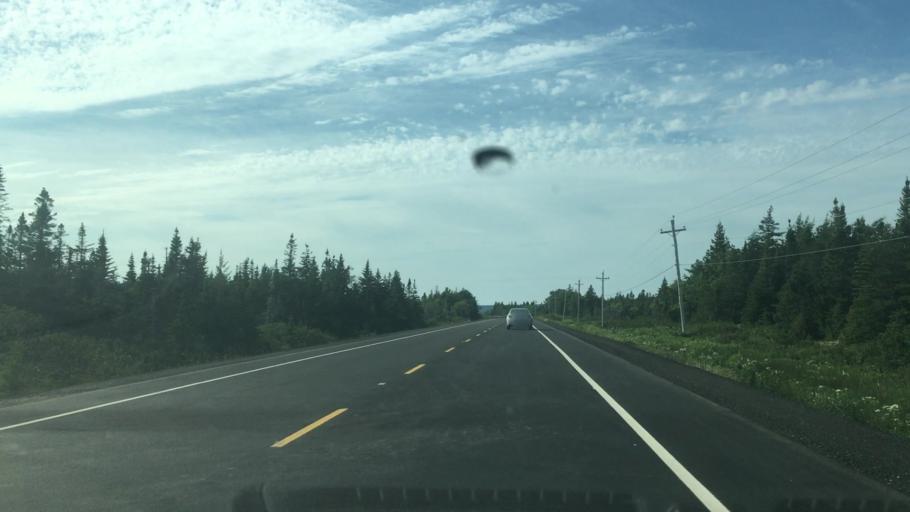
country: CA
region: Nova Scotia
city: Sydney Mines
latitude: 46.8469
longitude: -60.4126
